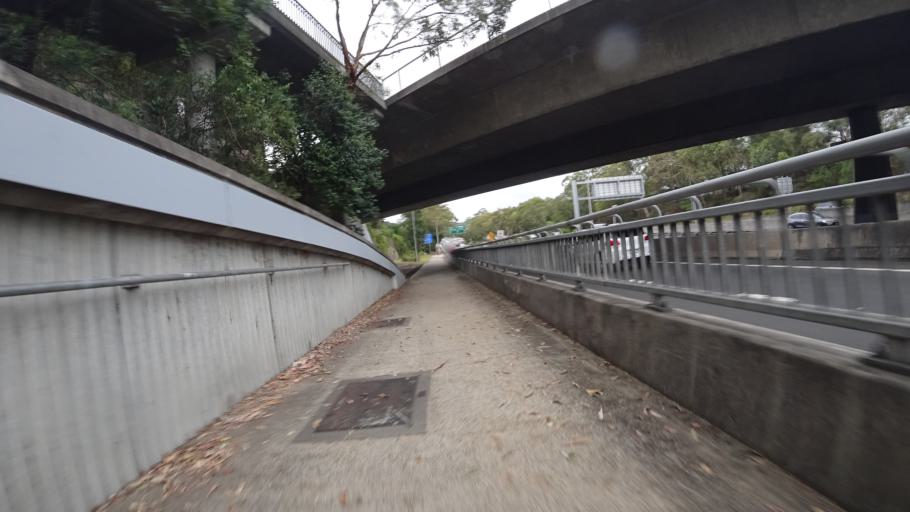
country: AU
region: New South Wales
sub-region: North Sydney
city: St Leonards
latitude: -33.8187
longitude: 151.2029
